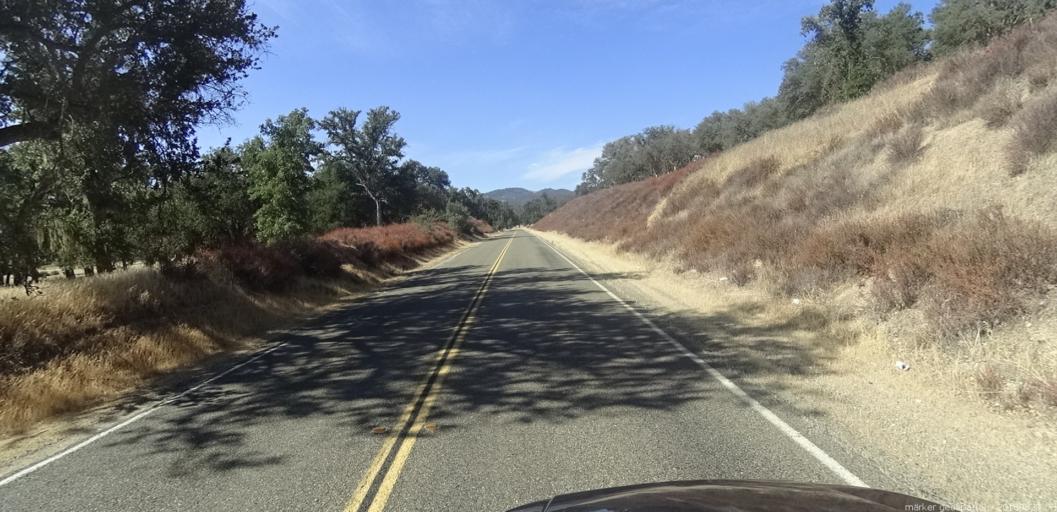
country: US
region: California
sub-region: San Luis Obispo County
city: Lake Nacimiento
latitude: 35.9029
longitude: -121.0882
